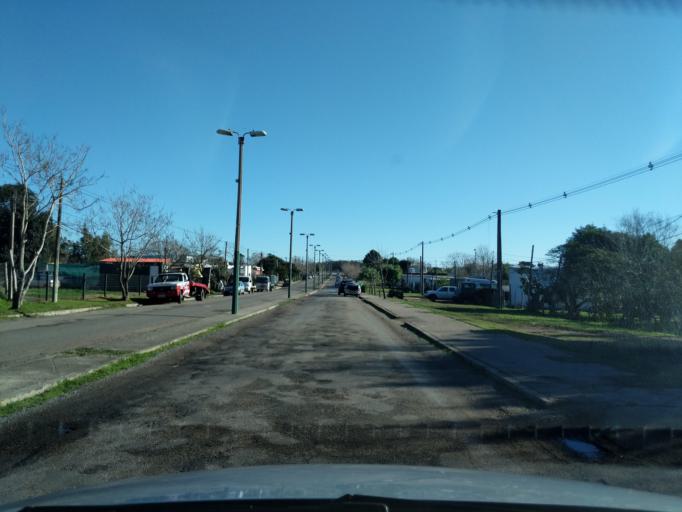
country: UY
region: Florida
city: Florida
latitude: -34.0942
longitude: -56.2370
